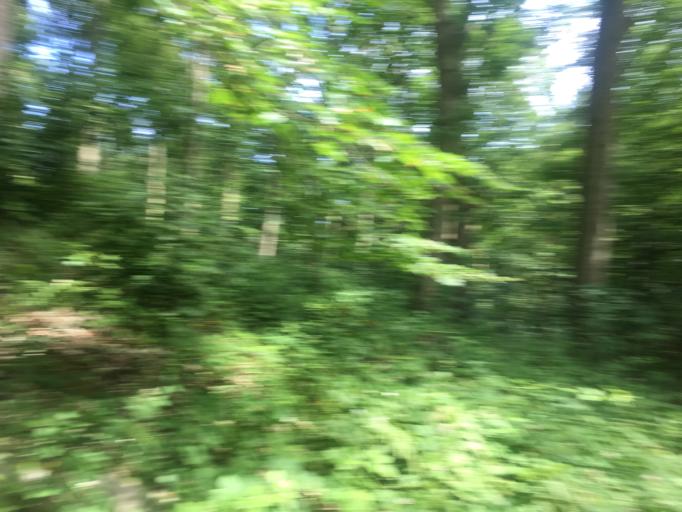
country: GB
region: England
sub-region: Sunderland
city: Washington
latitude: 54.8774
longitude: -1.5325
